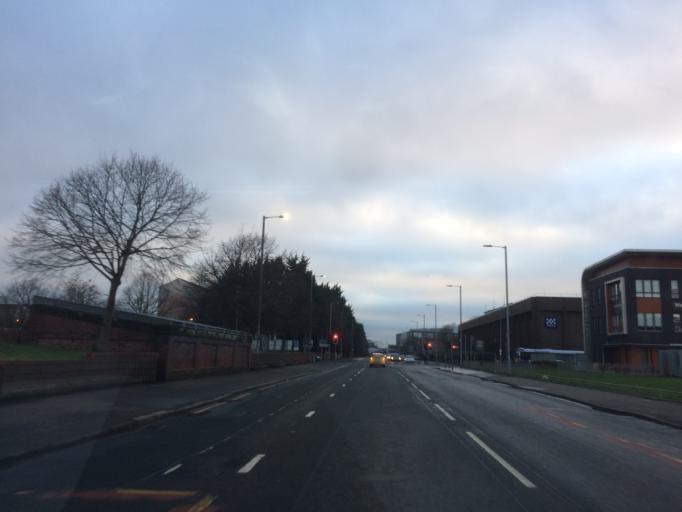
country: GB
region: Scotland
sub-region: South Lanarkshire
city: Rutherglen
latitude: 55.8487
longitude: -4.2147
